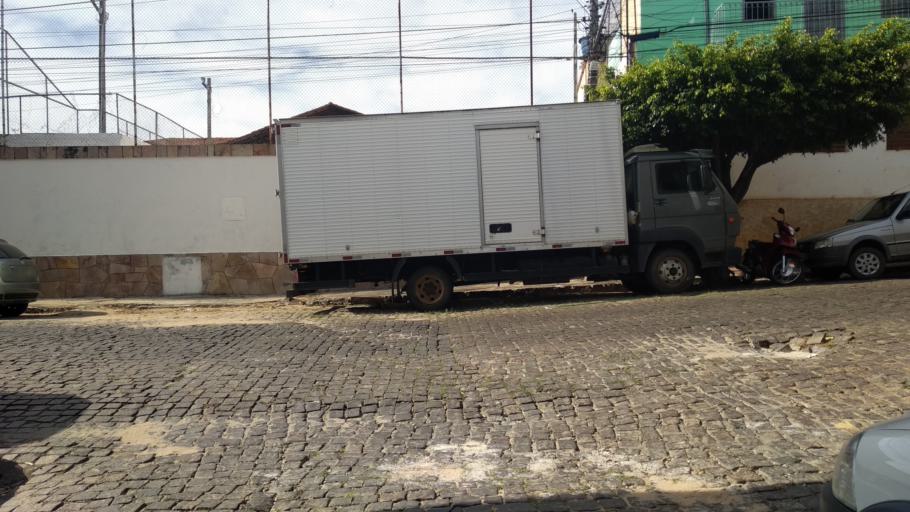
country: BR
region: Bahia
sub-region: Caetite
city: Caetite
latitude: -14.0672
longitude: -42.4916
